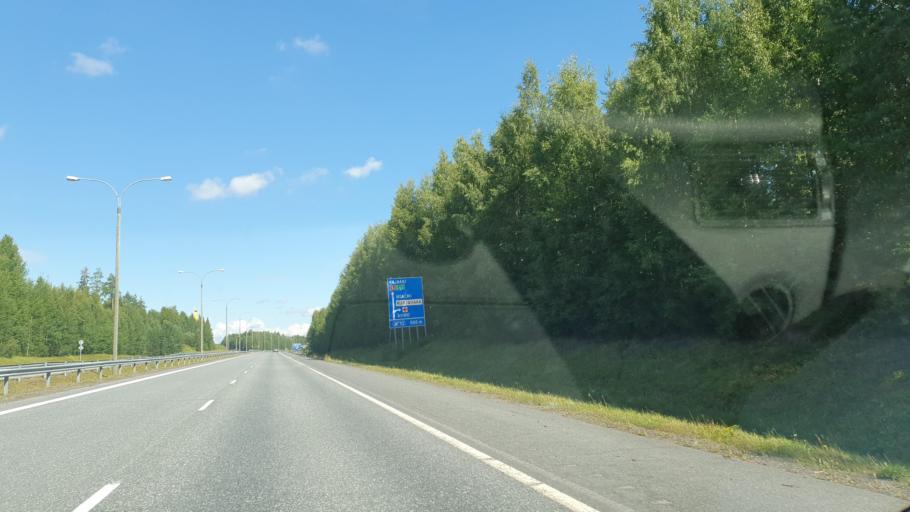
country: FI
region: Northern Savo
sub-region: Ylae-Savo
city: Iisalmi
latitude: 63.5385
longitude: 27.2478
